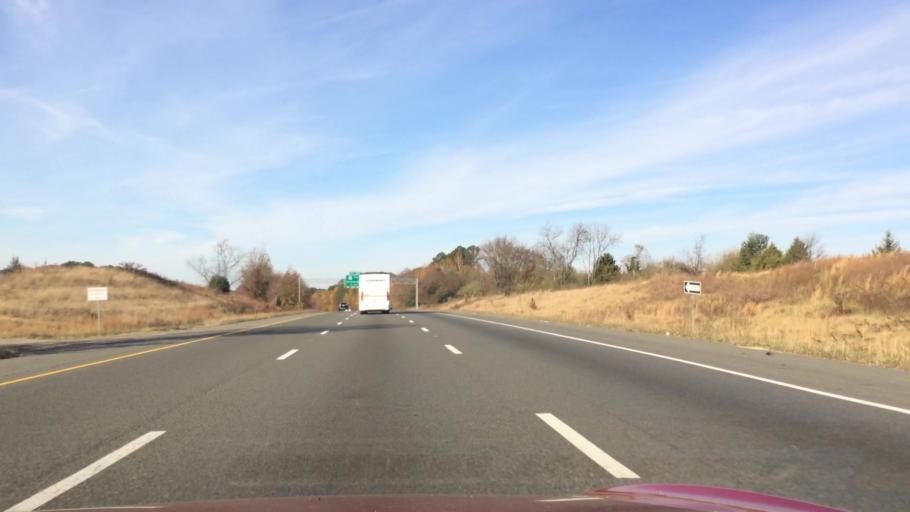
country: US
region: Virginia
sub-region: Henrico County
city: Glen Allen
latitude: 37.6821
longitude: -77.5240
